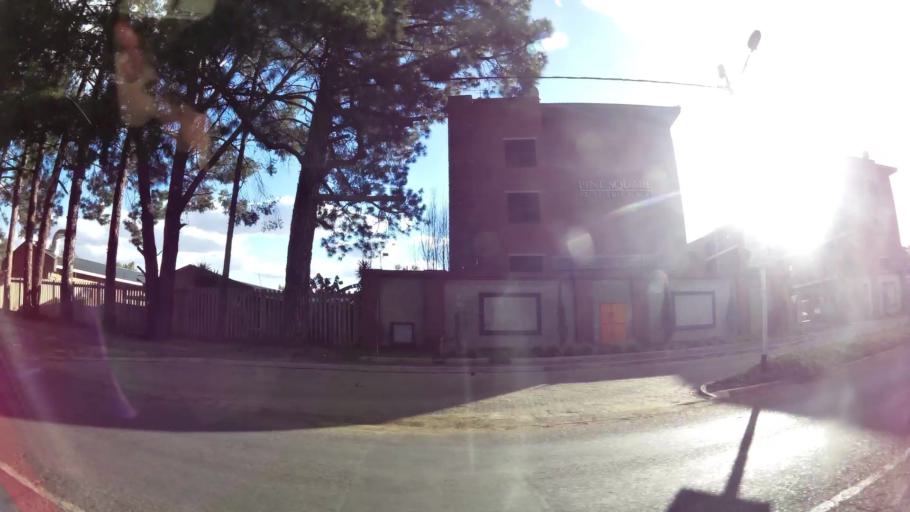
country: ZA
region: North-West
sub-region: Dr Kenneth Kaunda District Municipality
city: Potchefstroom
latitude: -26.6947
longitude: 27.0976
